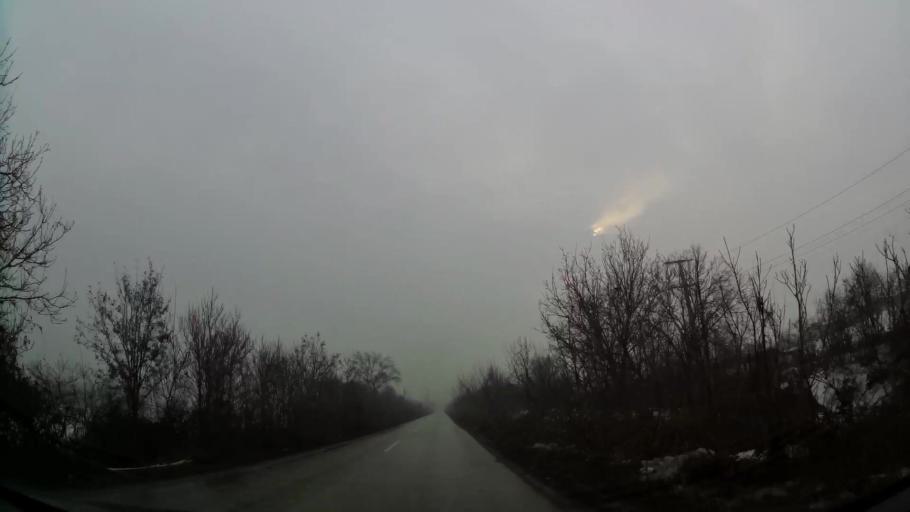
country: MK
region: Ilinden
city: Idrizovo
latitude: 41.9525
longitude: 21.5814
